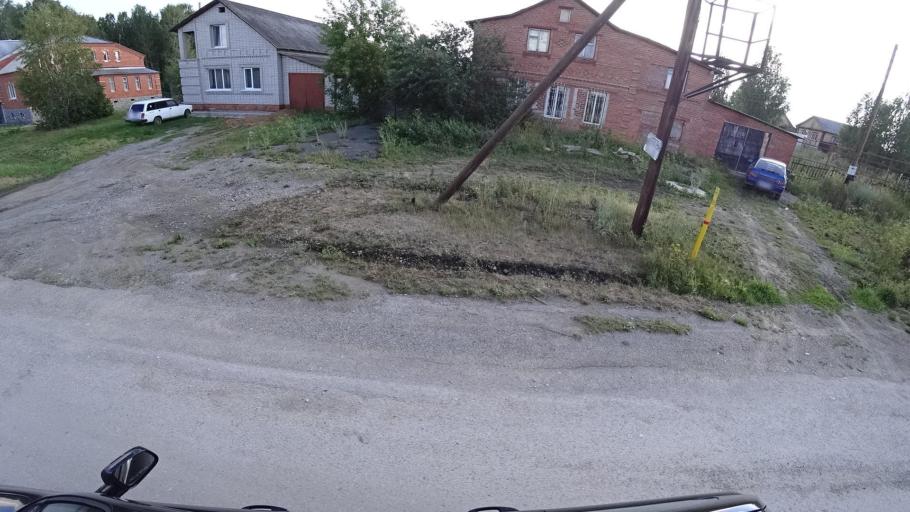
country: RU
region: Sverdlovsk
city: Obukhovskoye
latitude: 56.8500
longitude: 62.6529
